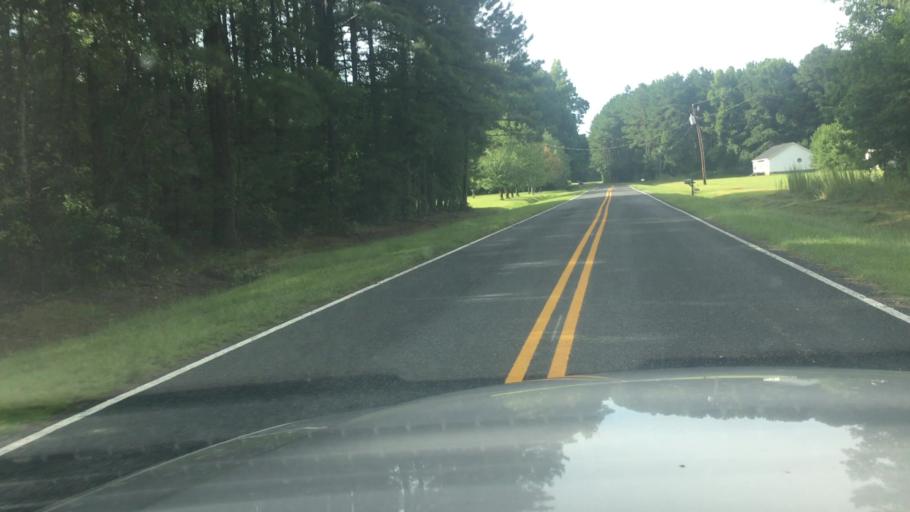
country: US
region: North Carolina
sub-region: Cumberland County
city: Eastover
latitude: 35.1570
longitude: -78.8532
